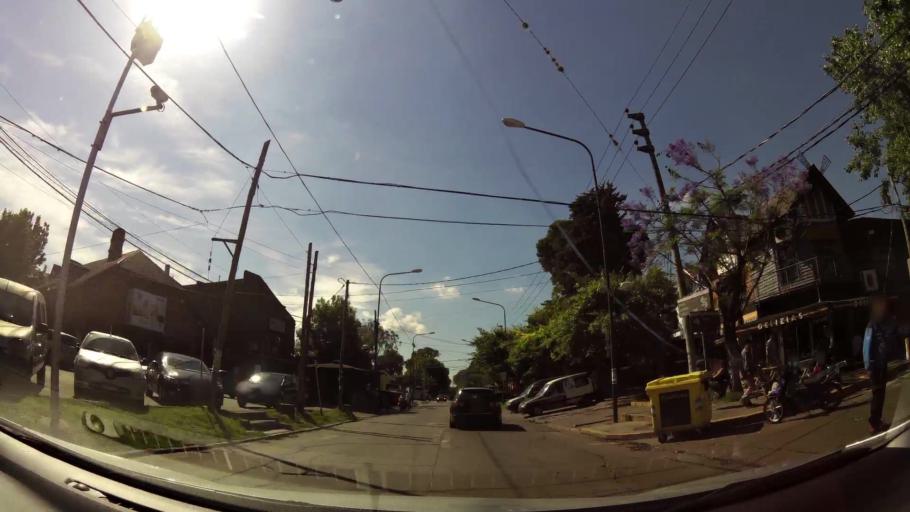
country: AR
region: Buenos Aires
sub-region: Partido de Tigre
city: Tigre
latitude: -34.4790
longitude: -58.5712
